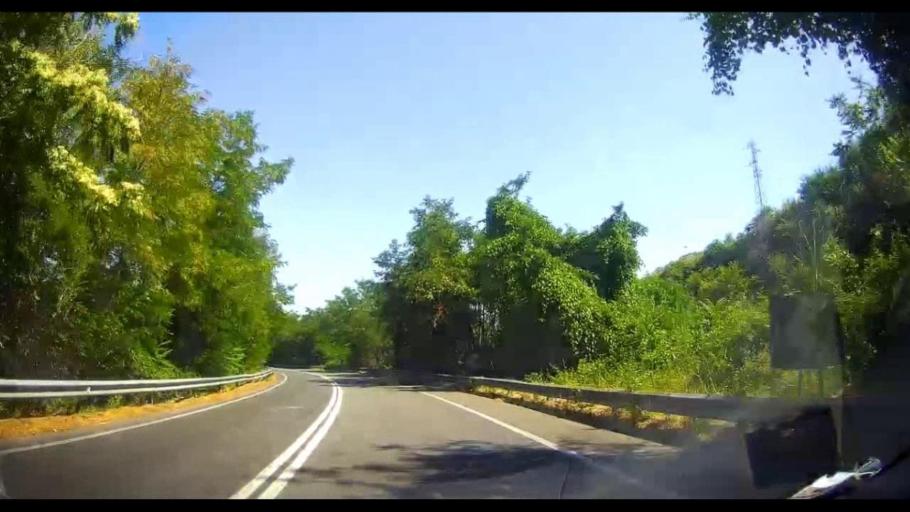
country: IT
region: Calabria
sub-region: Provincia di Cosenza
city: Cosenza
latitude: 39.2985
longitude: 16.2648
